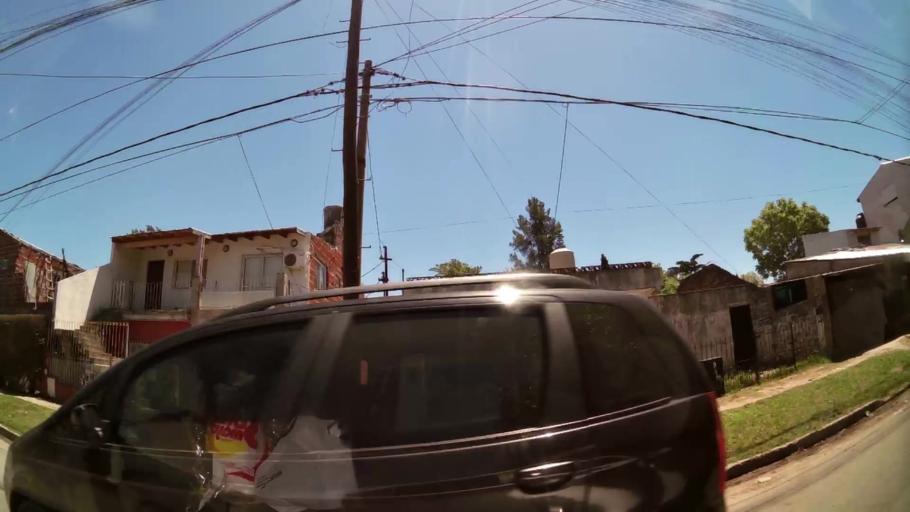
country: AR
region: Buenos Aires
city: Hurlingham
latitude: -34.5099
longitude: -58.7136
